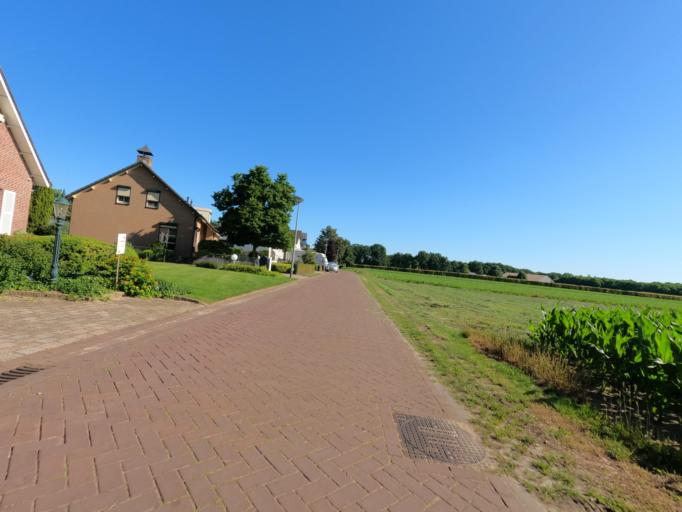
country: NL
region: Limburg
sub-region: Gemeente Roerdalen
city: Vlodrop
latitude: 51.1384
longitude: 6.0968
